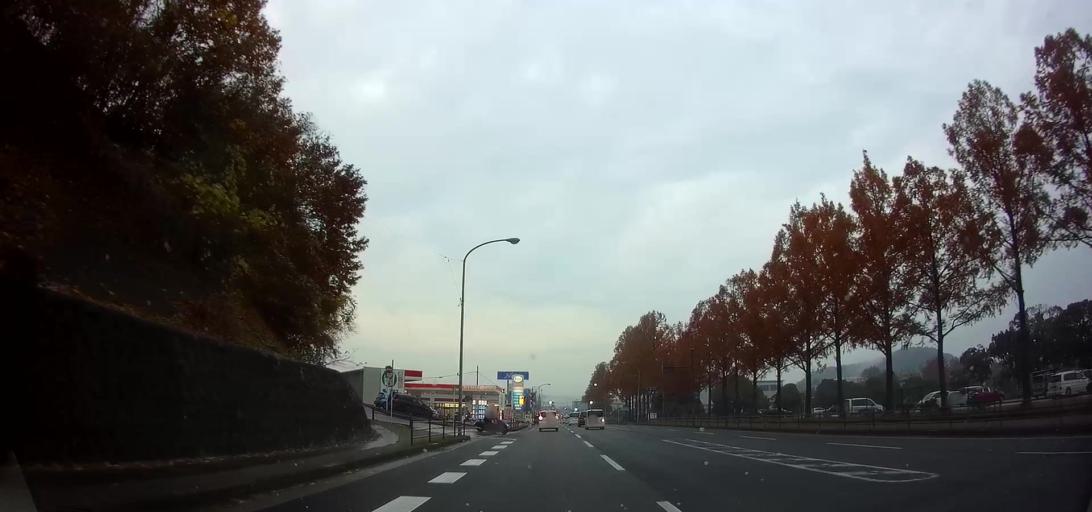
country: JP
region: Nagasaki
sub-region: Isahaya-shi
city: Isahaya
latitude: 32.8370
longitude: 130.0381
